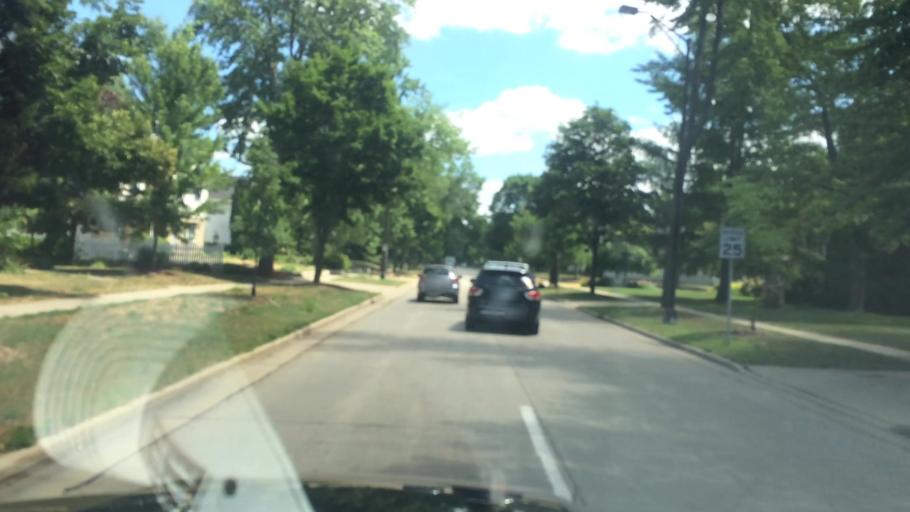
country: US
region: Wisconsin
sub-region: Portage County
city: Stevens Point
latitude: 44.5224
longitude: -89.5742
